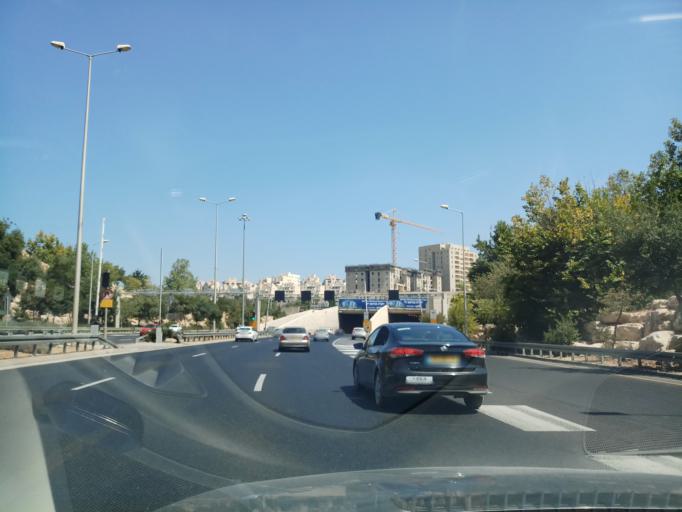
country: IL
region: Jerusalem
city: Jerusalem
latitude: 31.7634
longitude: 35.1933
